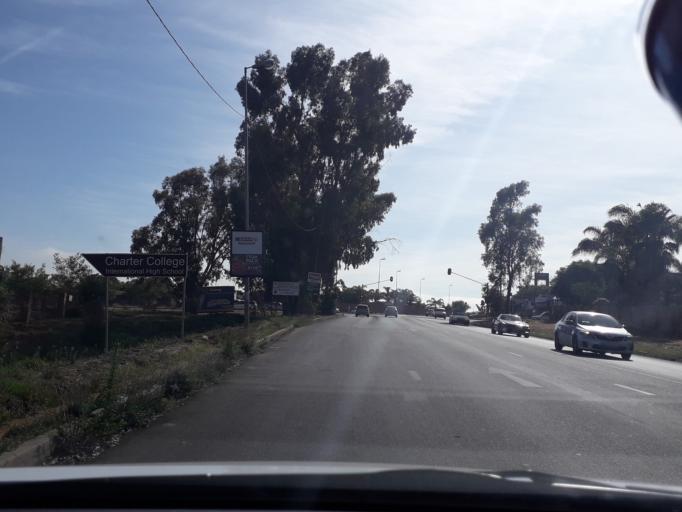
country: ZA
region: Gauteng
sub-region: City of Johannesburg Metropolitan Municipality
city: Roodepoort
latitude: -26.1005
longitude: 27.9034
